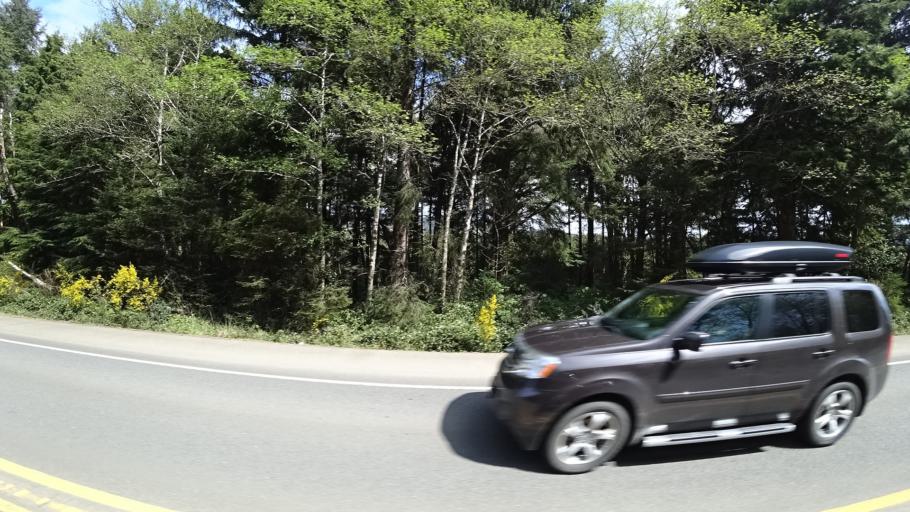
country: US
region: Oregon
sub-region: Lincoln County
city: Lincoln Beach
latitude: 44.8732
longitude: -124.0341
